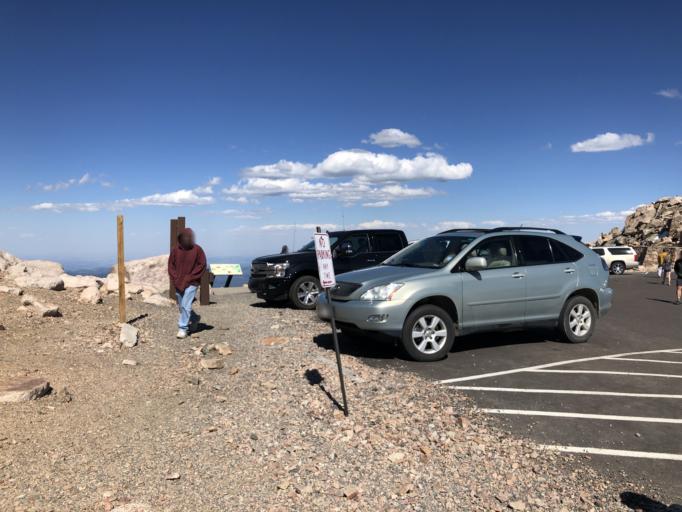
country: US
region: Colorado
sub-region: Clear Creek County
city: Georgetown
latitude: 39.5880
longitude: -105.6427
